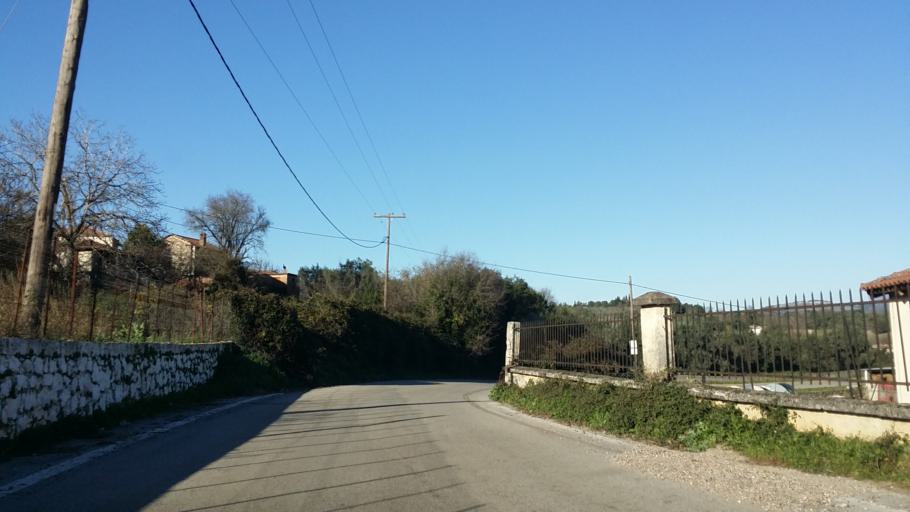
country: GR
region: West Greece
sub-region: Nomos Aitolias kai Akarnanias
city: Fitiai
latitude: 38.6313
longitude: 21.1529
